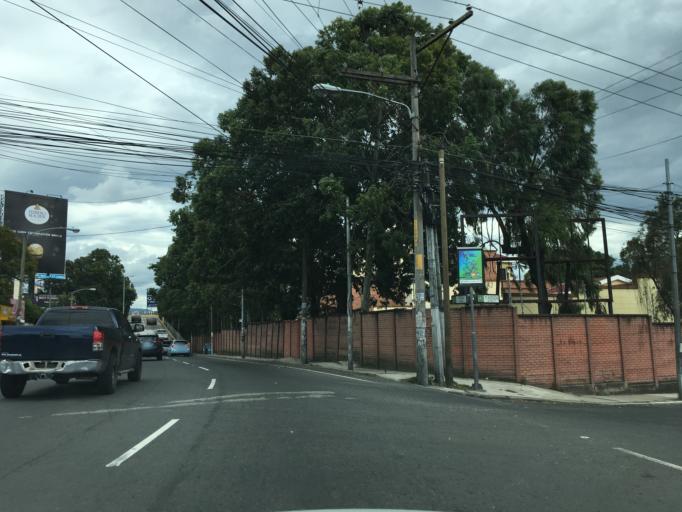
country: GT
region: Guatemala
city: Mixco
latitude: 14.5936
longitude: -90.5665
